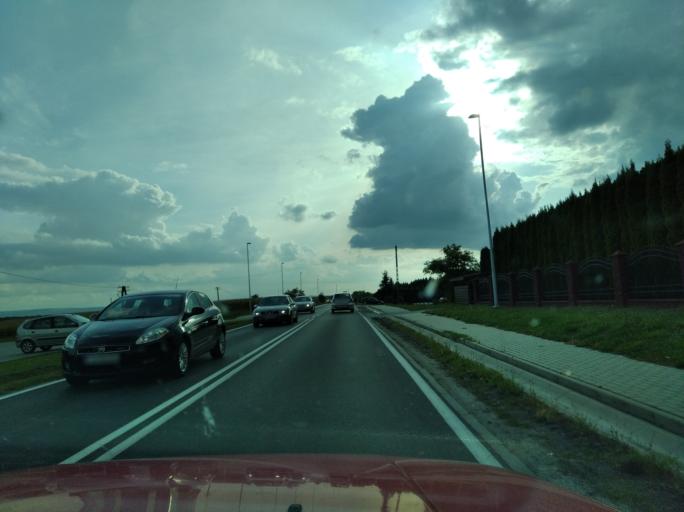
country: PL
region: Subcarpathian Voivodeship
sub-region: Powiat jaroslawski
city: Pawlosiow
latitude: 49.9871
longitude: 22.6575
